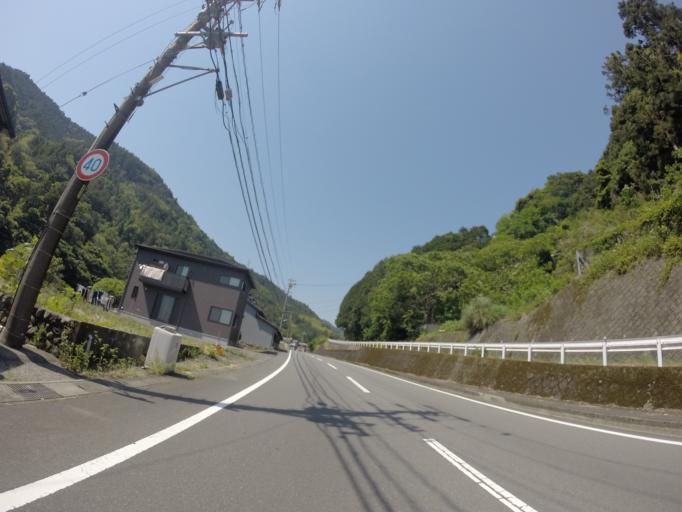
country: JP
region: Shizuoka
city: Fujinomiya
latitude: 35.1367
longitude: 138.5588
